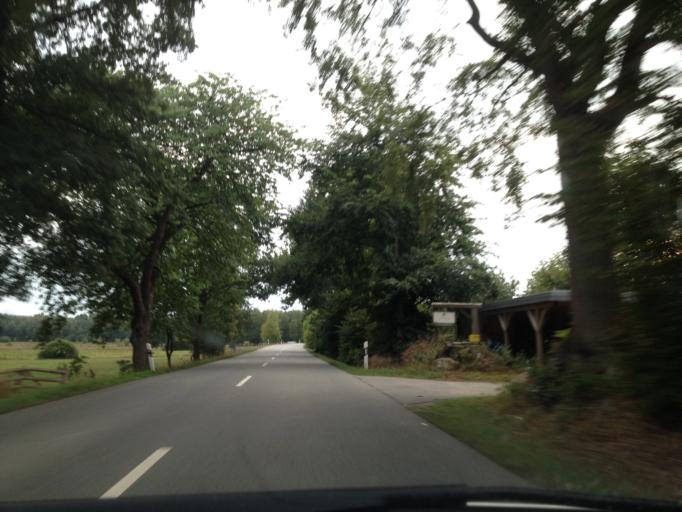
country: DE
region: Schleswig-Holstein
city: Daldorf
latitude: 54.0121
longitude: 10.2316
